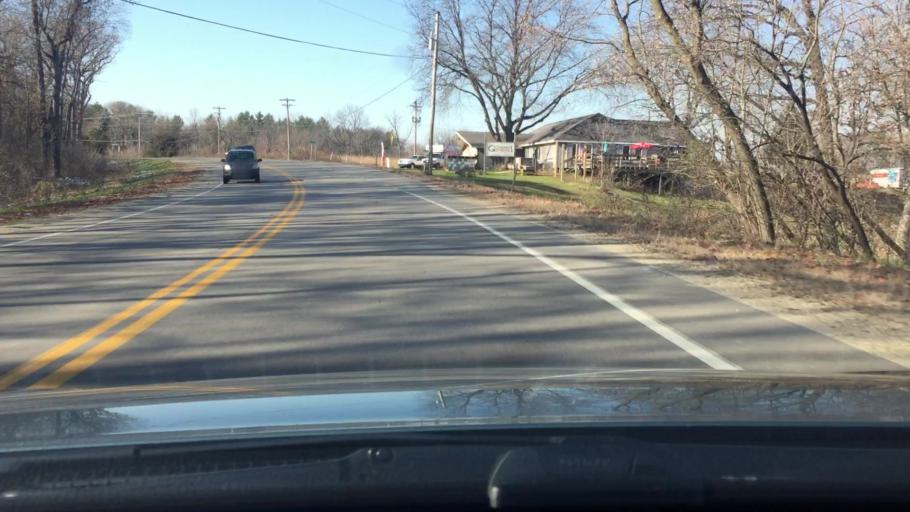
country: US
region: Wisconsin
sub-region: Jefferson County
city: Lake Ripley
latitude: 43.0128
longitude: -88.9918
